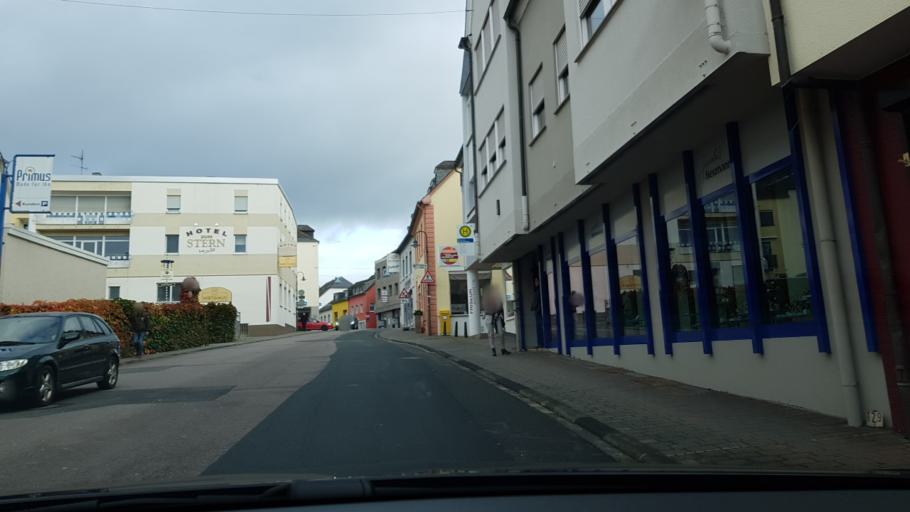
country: DE
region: Rheinland-Pfalz
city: Schweich
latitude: 49.8213
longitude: 6.7528
